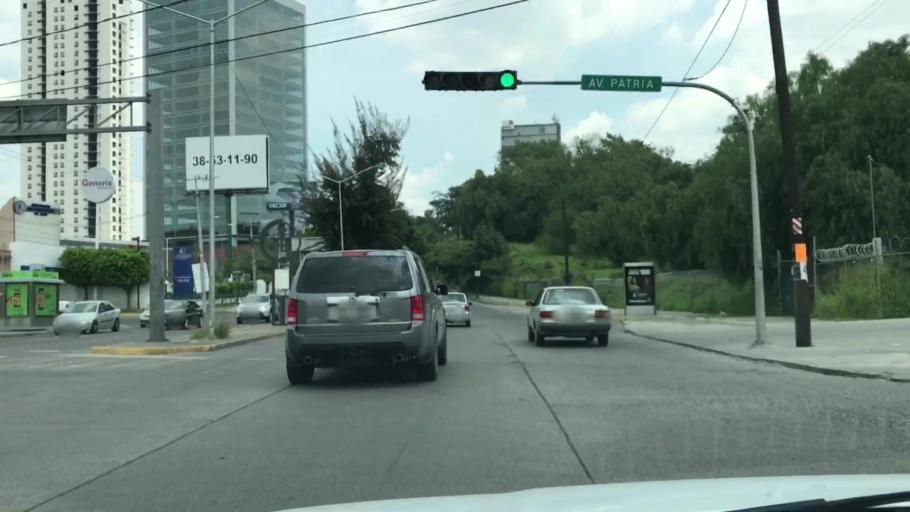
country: MX
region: Jalisco
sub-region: Zapopan
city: Zapopan
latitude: 20.7112
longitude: -103.3805
